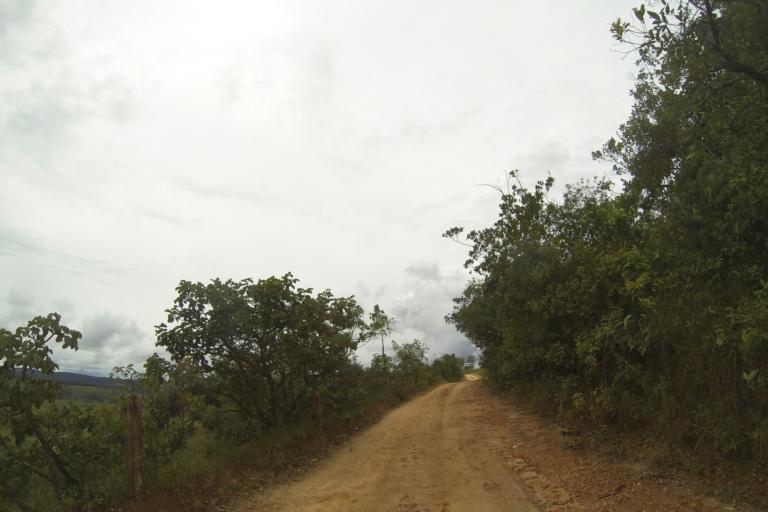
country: BR
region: Minas Gerais
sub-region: Ibia
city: Ibia
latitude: -19.6869
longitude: -46.6825
